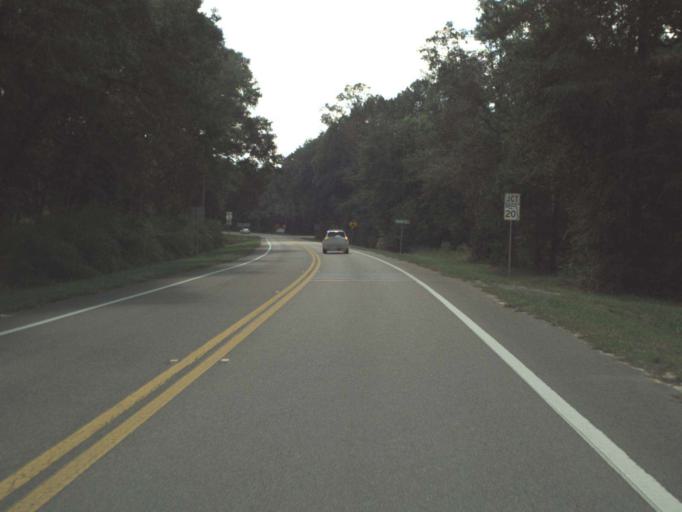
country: US
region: Florida
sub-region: Walton County
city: Freeport
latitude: 30.4753
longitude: -85.9630
